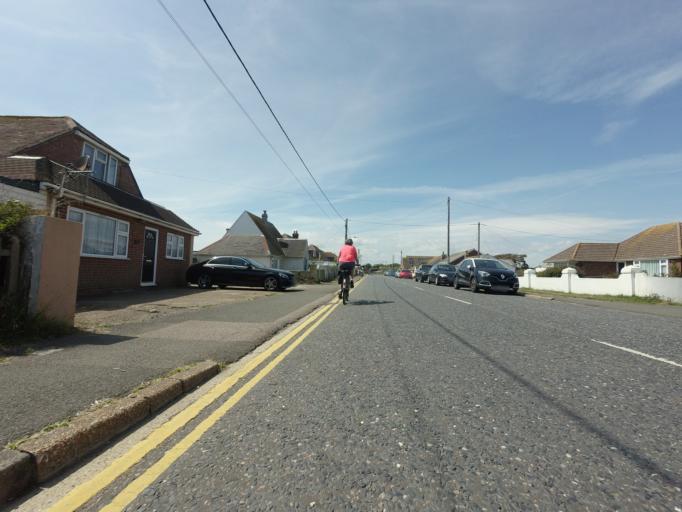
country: GB
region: England
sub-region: East Sussex
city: Rye
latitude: 50.9329
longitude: 0.8029
